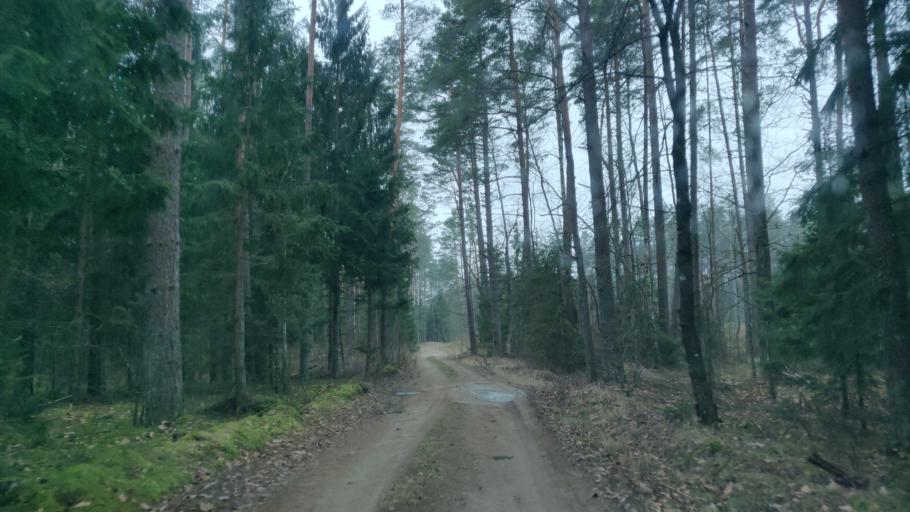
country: LT
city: Trakai
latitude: 54.5561
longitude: 24.9528
